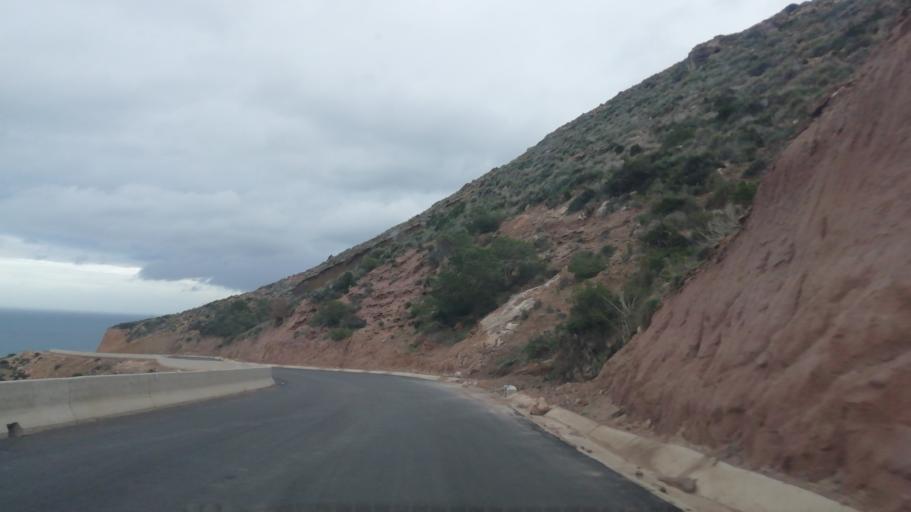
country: DZ
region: Oran
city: Bir el Djir
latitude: 35.7658
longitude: -0.5222
